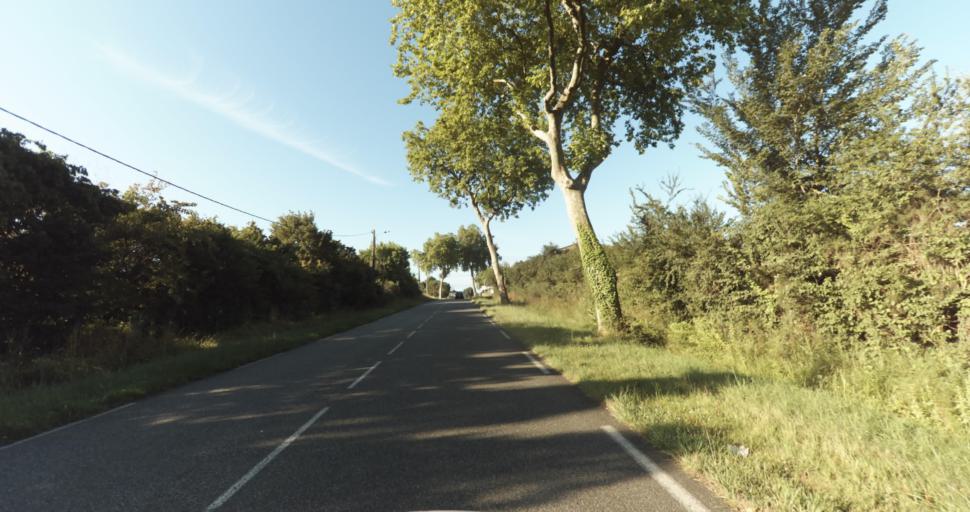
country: FR
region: Aquitaine
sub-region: Departement de la Gironde
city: Bazas
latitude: 44.4241
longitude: -0.2147
